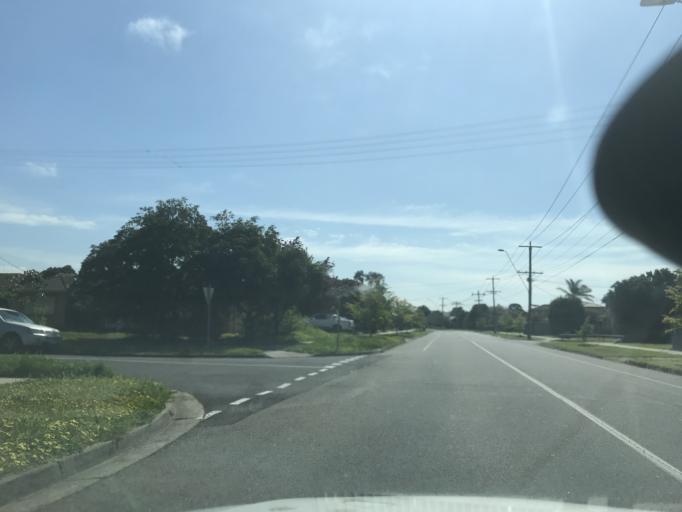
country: AU
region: Victoria
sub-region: Whittlesea
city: Epping
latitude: -37.6473
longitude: 145.0358
